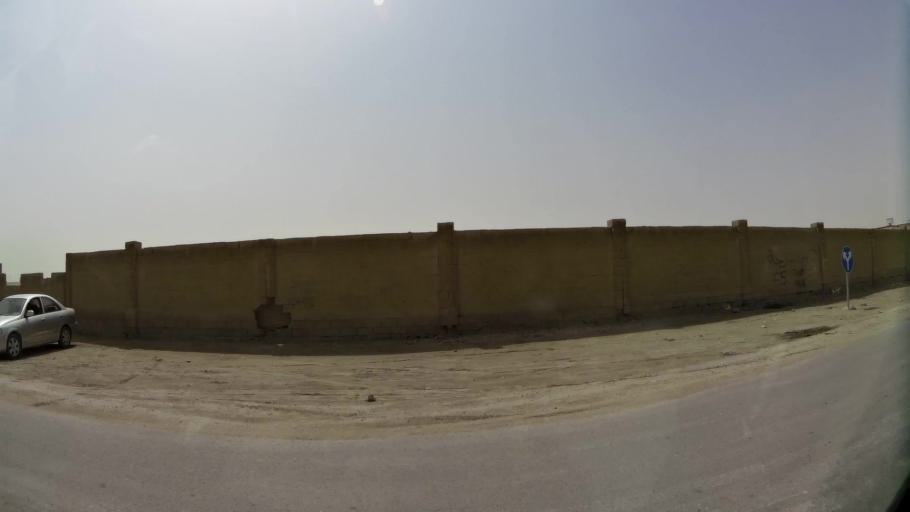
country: QA
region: Baladiyat ar Rayyan
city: Ar Rayyan
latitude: 25.2364
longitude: 51.4261
